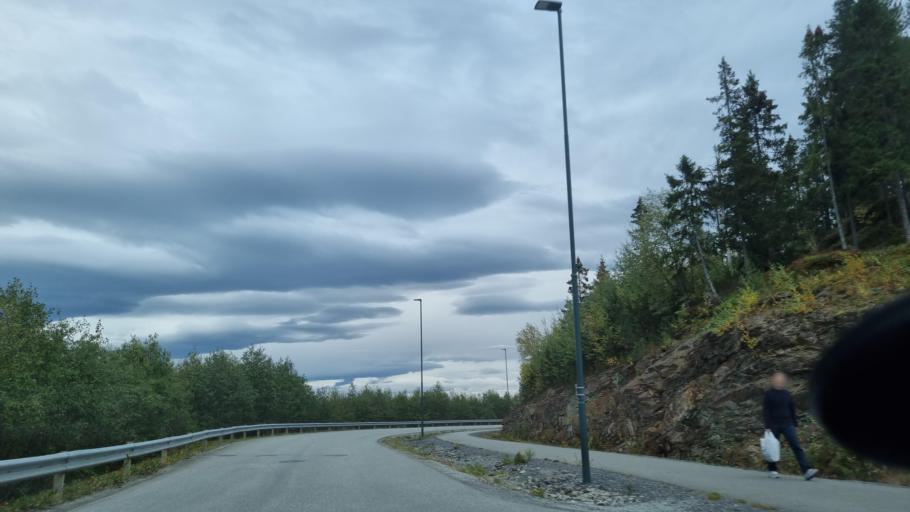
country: NO
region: Sor-Trondelag
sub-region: Malvik
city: Hommelvik
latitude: 63.4256
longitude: 10.7600
